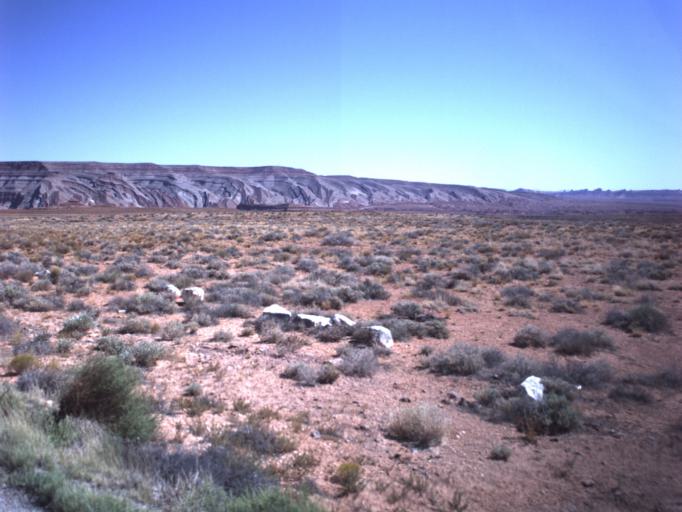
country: US
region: Arizona
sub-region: Navajo County
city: Kayenta
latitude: 37.2002
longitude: -109.8950
